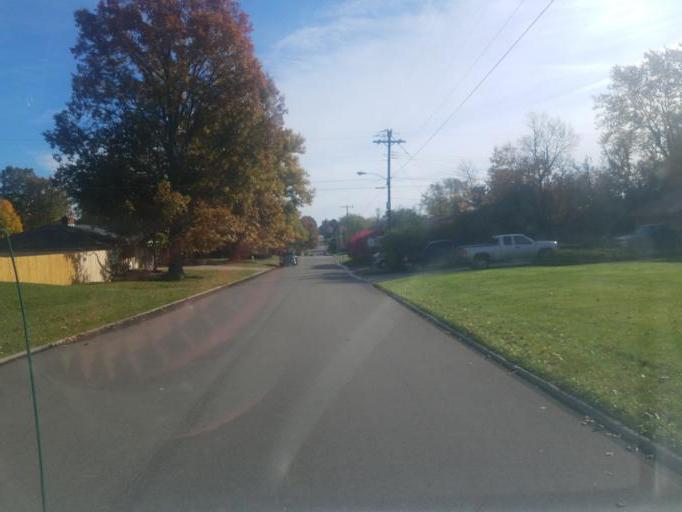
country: US
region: Ohio
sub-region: Richland County
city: Mansfield
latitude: 40.7295
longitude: -82.5315
